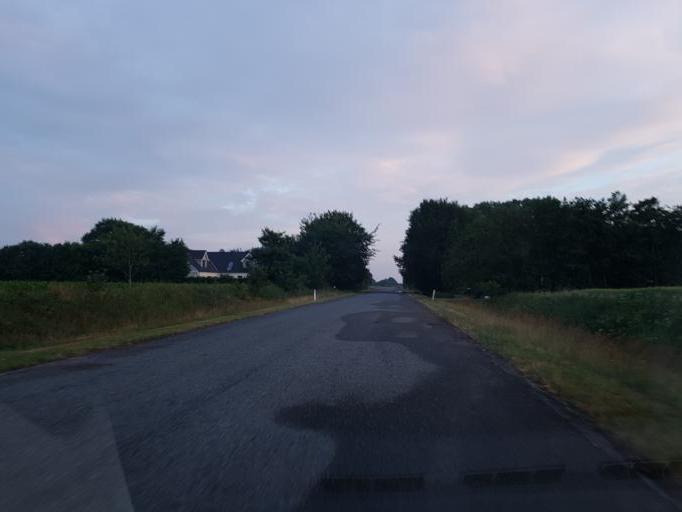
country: DK
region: South Denmark
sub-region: Esbjerg Kommune
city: Tjaereborg
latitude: 55.5185
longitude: 8.5706
